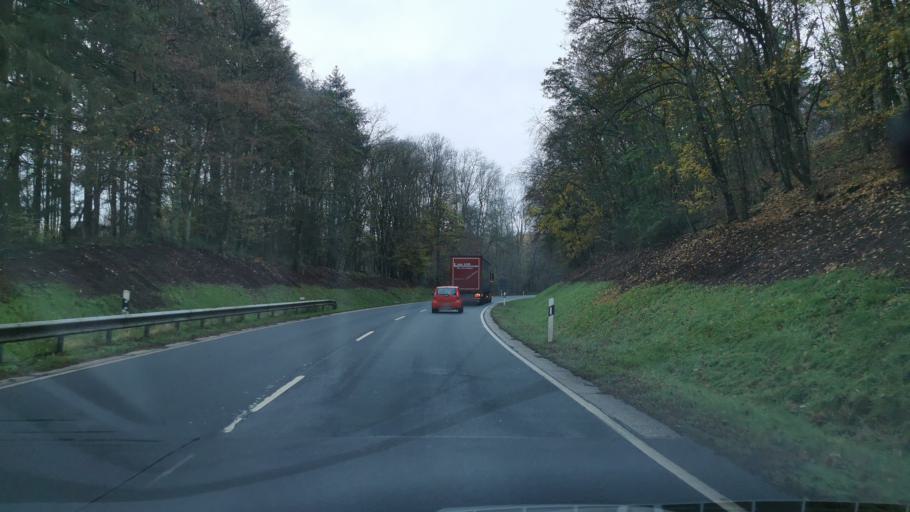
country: DE
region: Rheinland-Pfalz
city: Dohr
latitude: 50.1368
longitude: 7.1388
